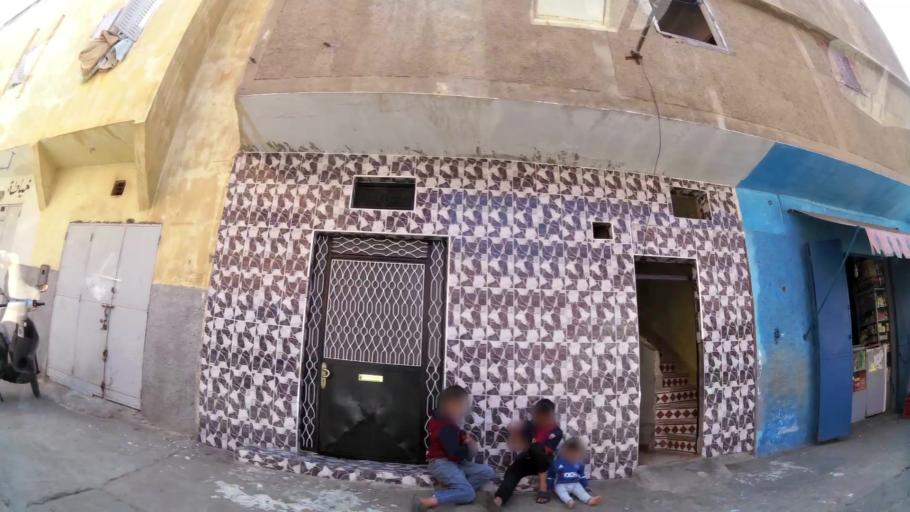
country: MA
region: Gharb-Chrarda-Beni Hssen
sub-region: Kenitra Province
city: Kenitra
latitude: 34.2516
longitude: -6.5549
